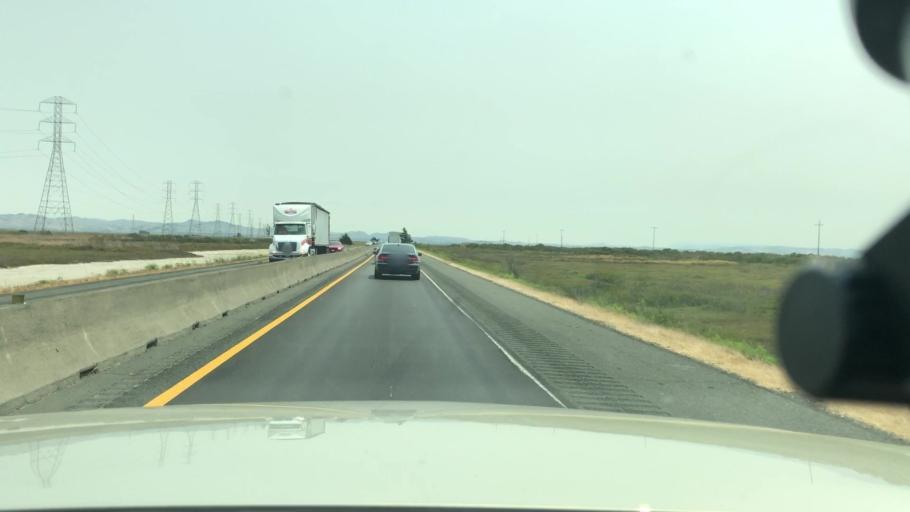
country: US
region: California
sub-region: Marin County
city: Black Point-Green Point
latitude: 38.1538
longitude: -122.3975
